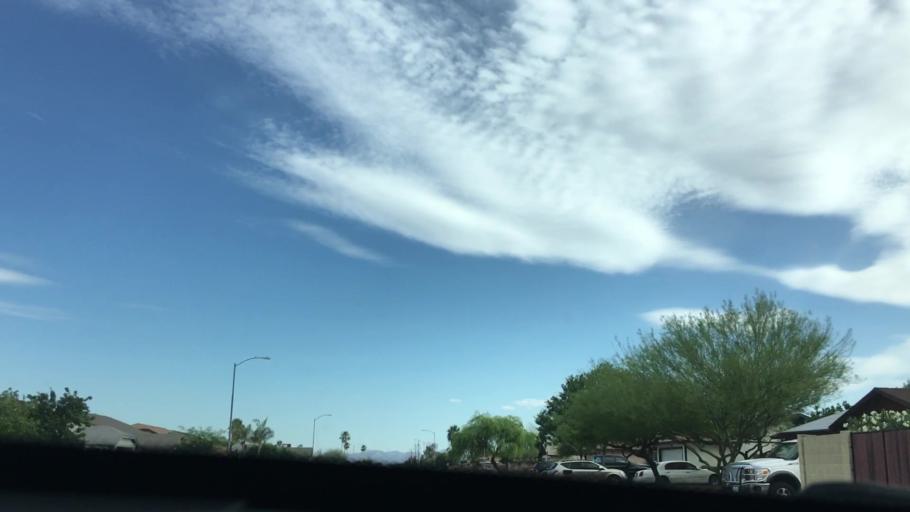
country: US
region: Arizona
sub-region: Maricopa County
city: Peoria
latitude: 33.5878
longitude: -112.2291
